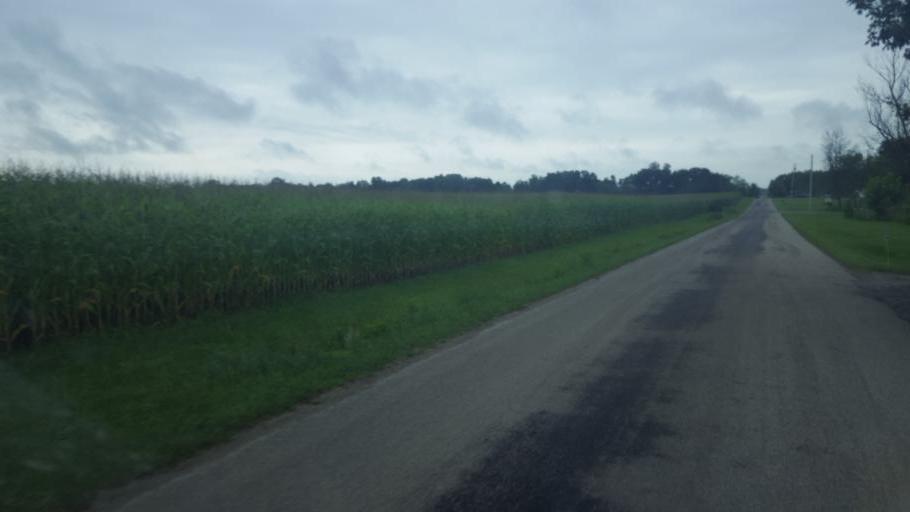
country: US
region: Ohio
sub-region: Knox County
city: Centerburg
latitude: 40.3965
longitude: -82.7409
